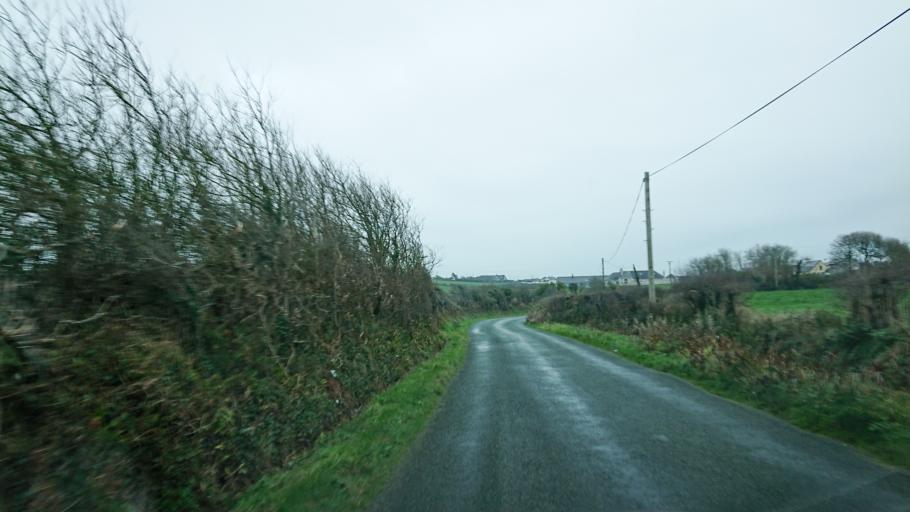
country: IE
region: Munster
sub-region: Waterford
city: Dunmore East
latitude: 52.1467
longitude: -7.0567
